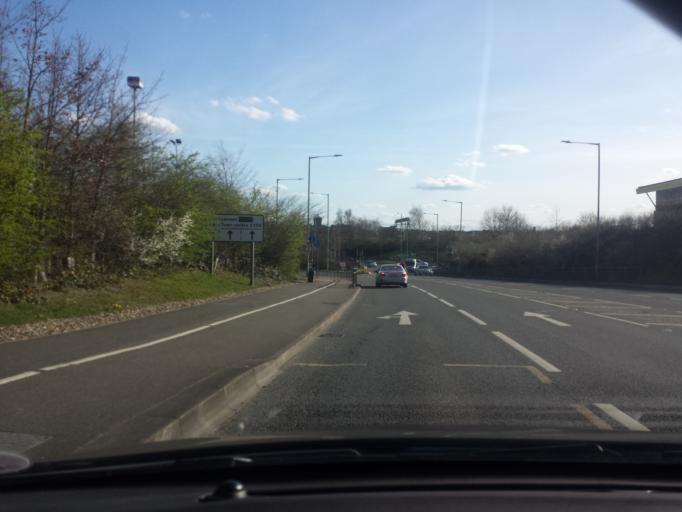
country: GB
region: England
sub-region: Essex
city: Colchester
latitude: 51.9018
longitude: 0.8969
